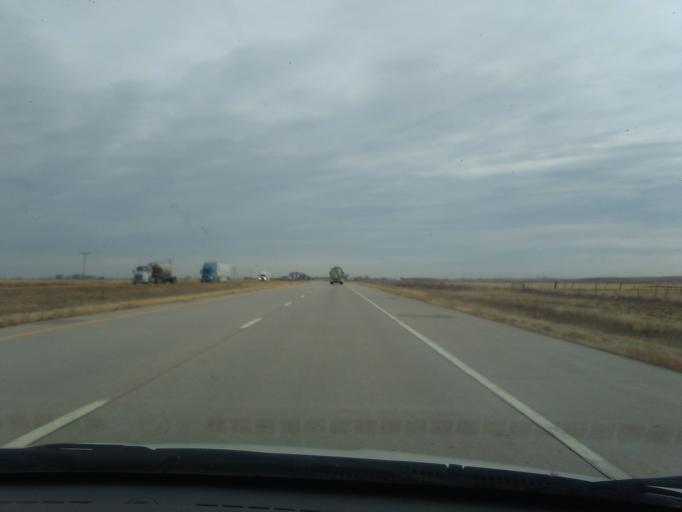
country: US
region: Colorado
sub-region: Morgan County
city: Fort Morgan
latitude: 40.2320
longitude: -104.1232
